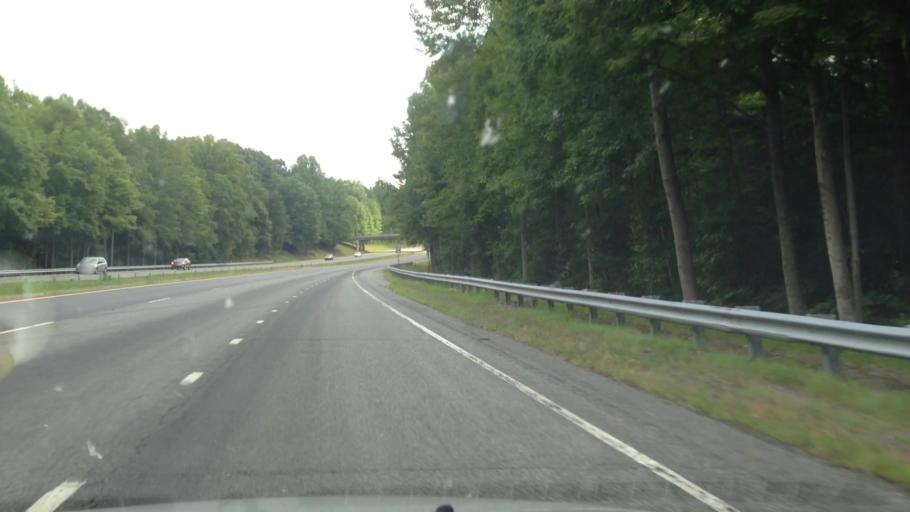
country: US
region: North Carolina
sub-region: Rockingham County
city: Reidsville
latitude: 36.4406
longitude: -79.5713
